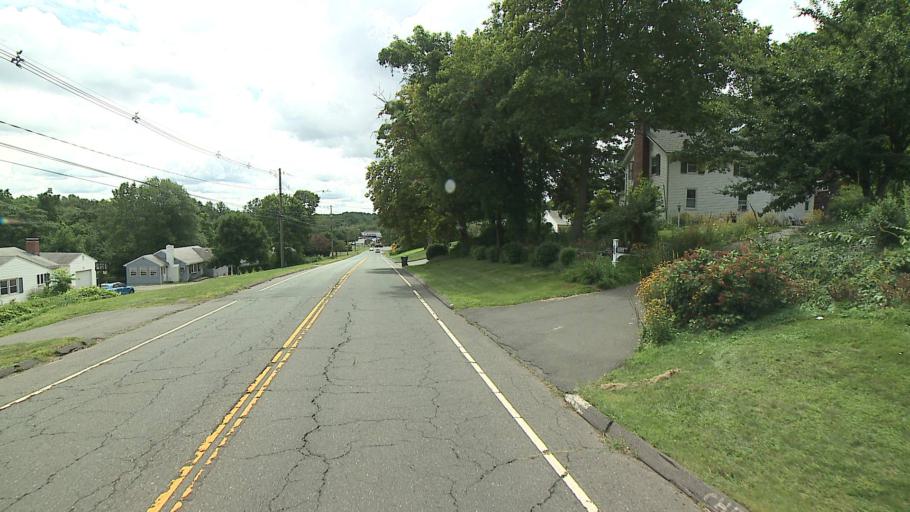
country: US
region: Connecticut
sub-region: Hartford County
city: Kensington
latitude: 41.6380
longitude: -72.7885
